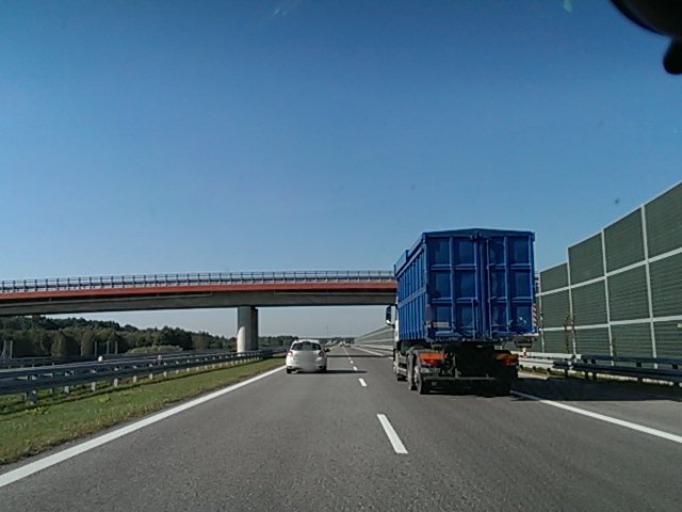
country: PL
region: Subcarpathian Voivodeship
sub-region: Powiat rzeszowski
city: Trzciana
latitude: 50.1159
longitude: 21.7774
